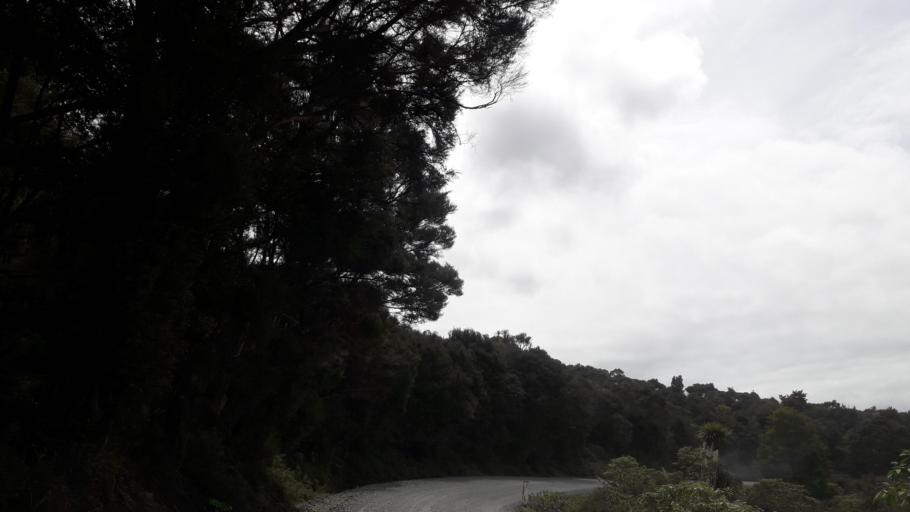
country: NZ
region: Northland
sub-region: Far North District
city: Taipa
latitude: -35.0372
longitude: 173.5650
